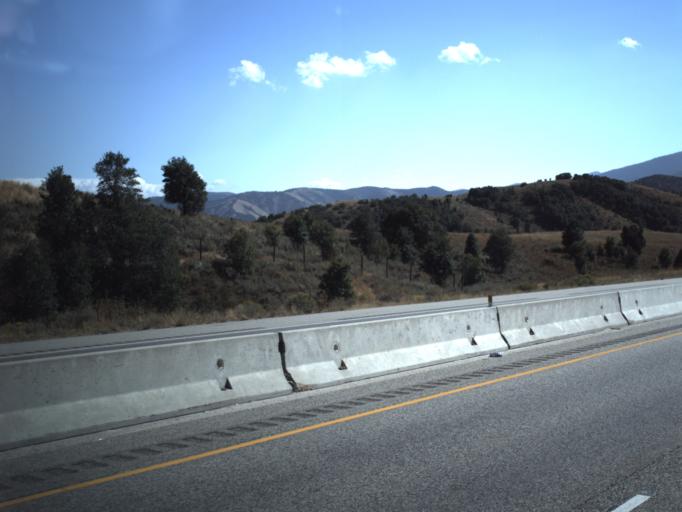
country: US
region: Utah
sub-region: Box Elder County
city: Brigham City
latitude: 41.5429
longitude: -111.9567
